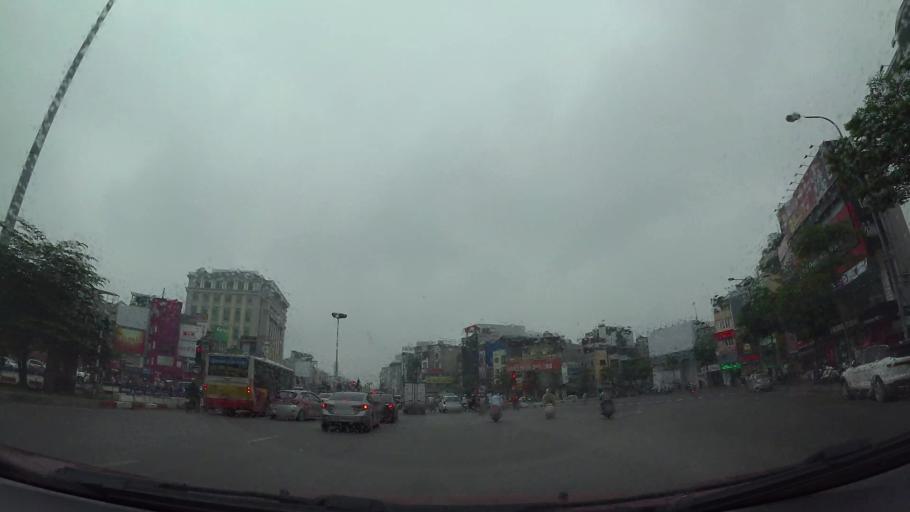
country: VN
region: Ha Noi
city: Dong Da
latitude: 21.0186
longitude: 105.8292
